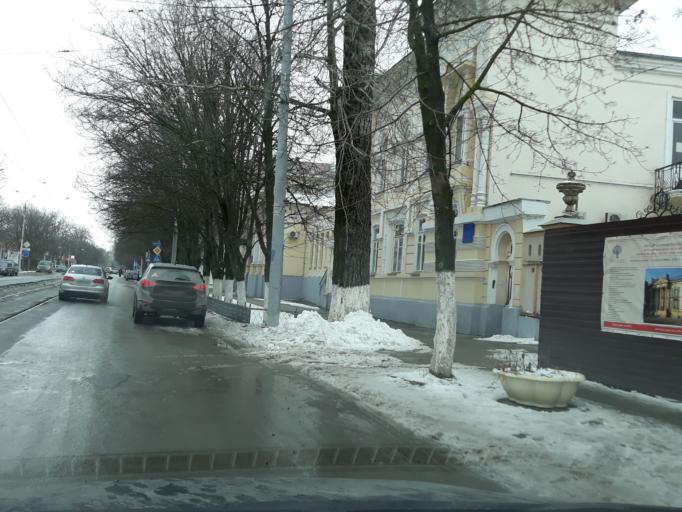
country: RU
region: Rostov
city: Taganrog
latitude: 47.2136
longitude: 38.9286
